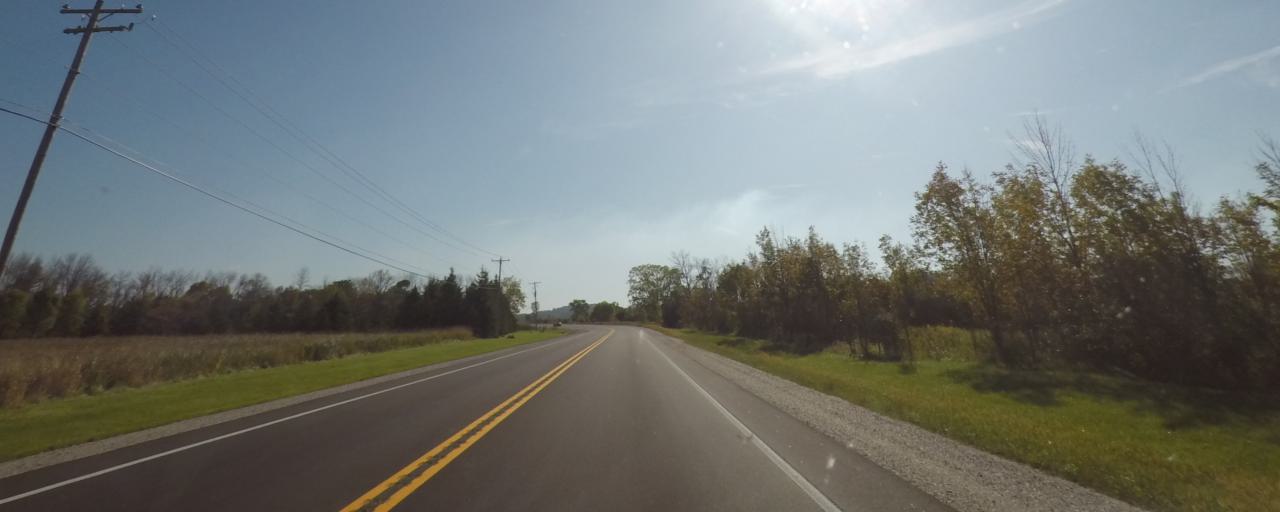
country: US
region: Wisconsin
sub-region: Jefferson County
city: Jefferson
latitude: 43.0125
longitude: -88.7563
